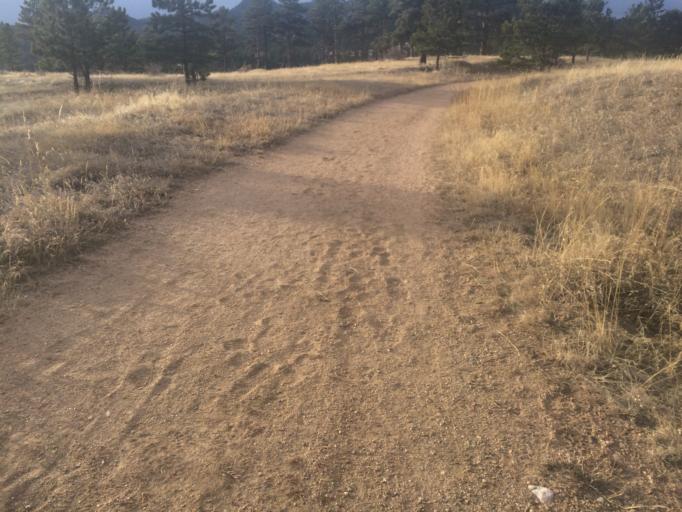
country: US
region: Colorado
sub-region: Boulder County
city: Coal Creek
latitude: 39.9583
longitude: -105.3413
